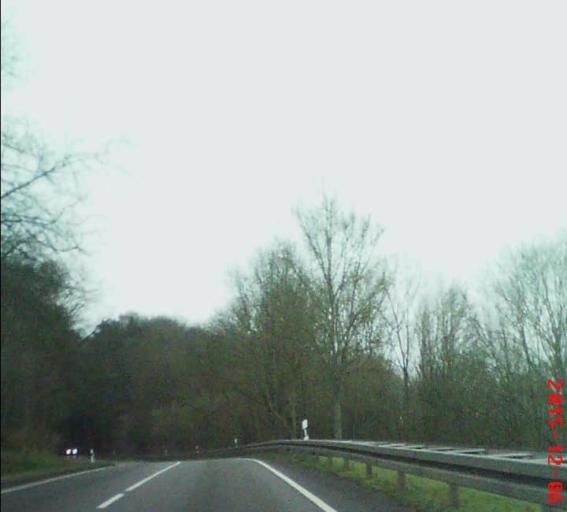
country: DE
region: Thuringia
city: Obermassfeld-Grimmenthal
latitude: 50.5235
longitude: 10.4504
